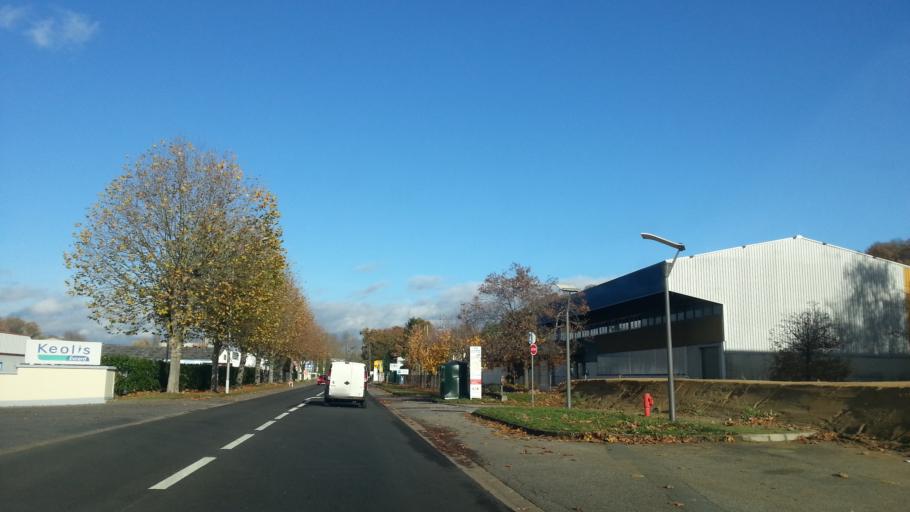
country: FR
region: Picardie
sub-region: Departement de l'Oise
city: Creil
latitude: 49.2714
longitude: 2.4957
